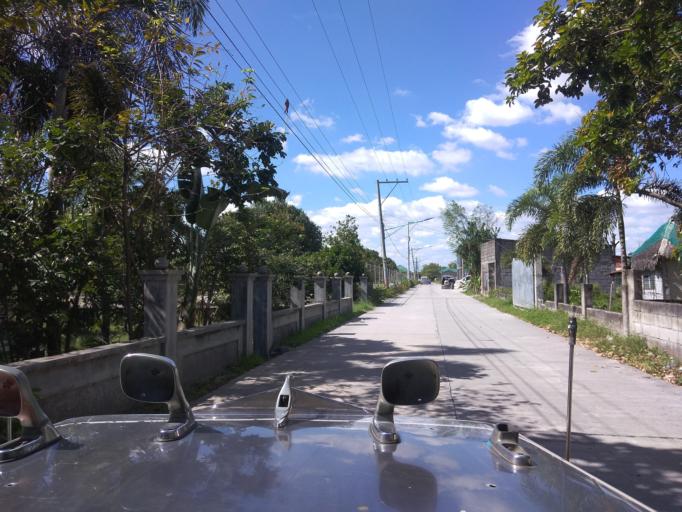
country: PH
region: Central Luzon
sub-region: Province of Pampanga
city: Bacolor
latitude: 15.0070
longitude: 120.6470
